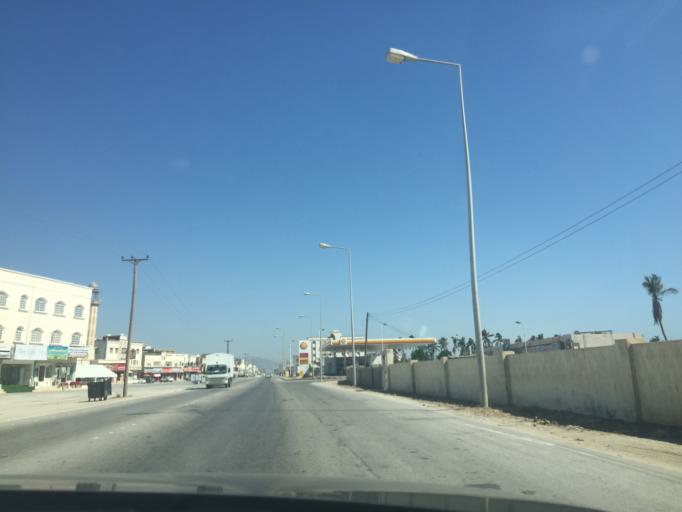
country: OM
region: Zufar
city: Salalah
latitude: 17.0190
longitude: 54.1592
